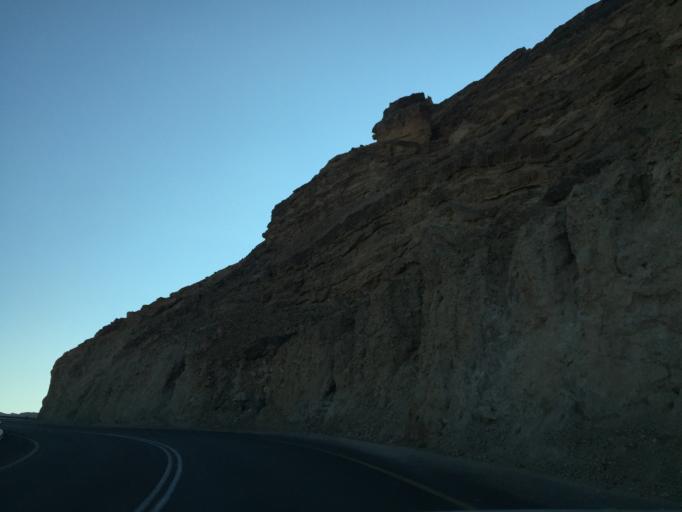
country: IL
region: Southern District
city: Mitzpe Ramon
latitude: 30.3209
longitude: 34.9578
